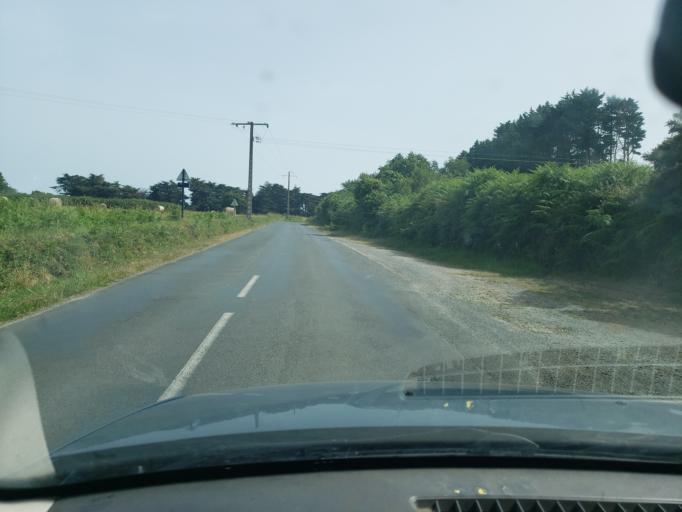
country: FR
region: Brittany
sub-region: Departement du Finistere
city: Plobannalec-Lesconil
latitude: 47.8070
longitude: -4.2298
